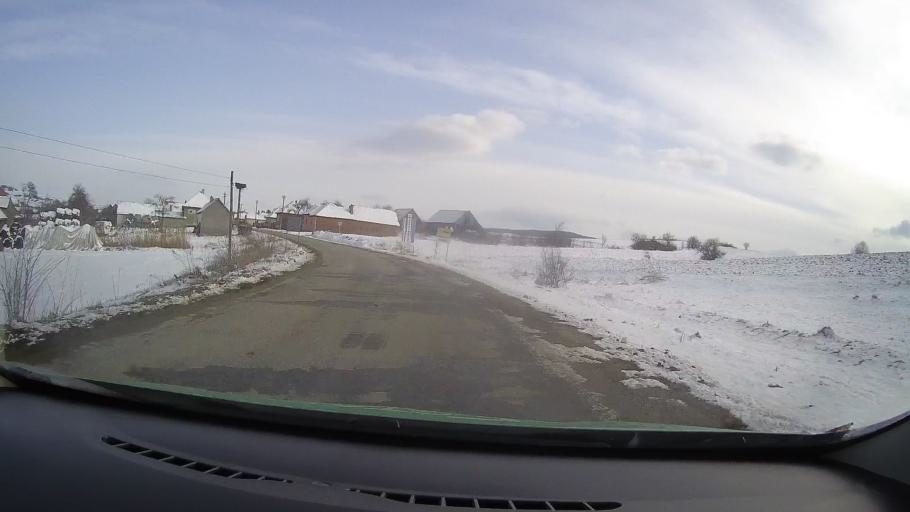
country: RO
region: Sibiu
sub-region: Comuna Merghindeal
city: Merghindeal
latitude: 45.9680
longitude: 24.7121
